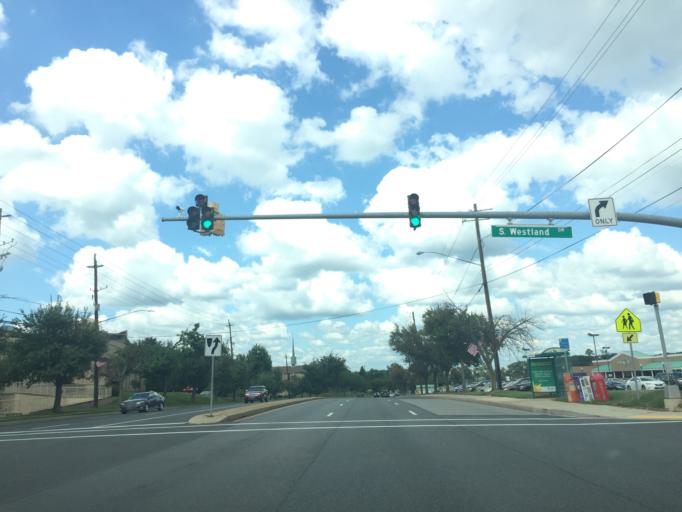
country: US
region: Maryland
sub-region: Montgomery County
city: Derwood
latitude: 39.1260
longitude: -77.1827
